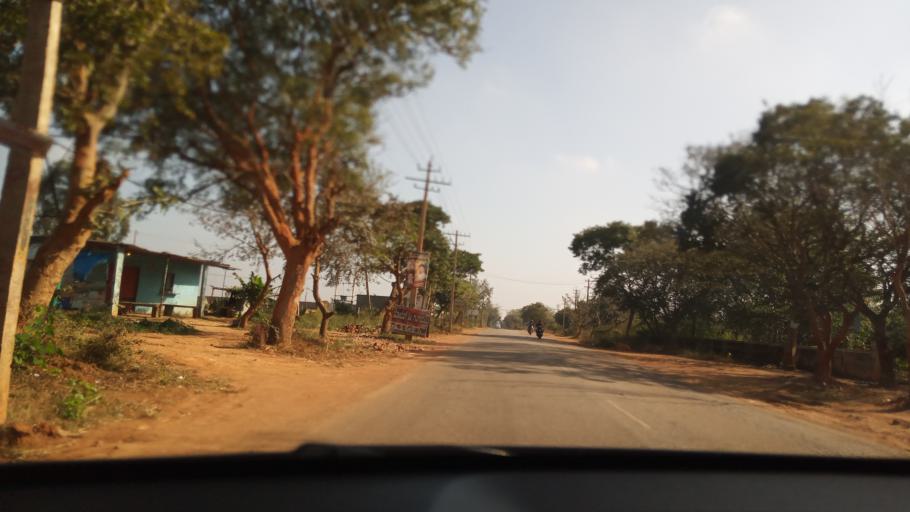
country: IN
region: Karnataka
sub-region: Bangalore Rural
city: Devanhalli
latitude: 13.2588
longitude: 77.7286
